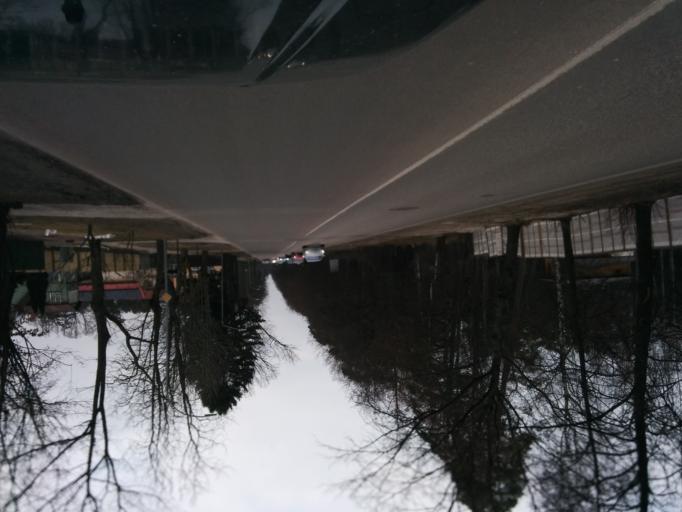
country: LV
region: Jurmala
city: Jurmala
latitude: 56.9586
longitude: 23.6817
